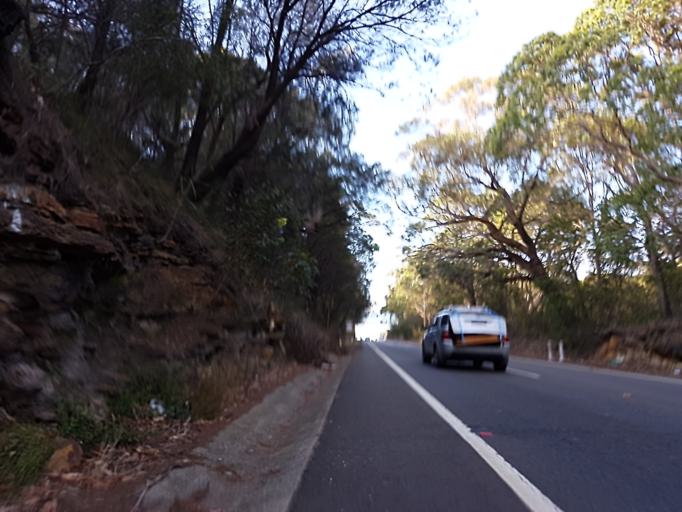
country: AU
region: New South Wales
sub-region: Warringah
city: Allambie Heights
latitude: -33.7573
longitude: 151.2332
